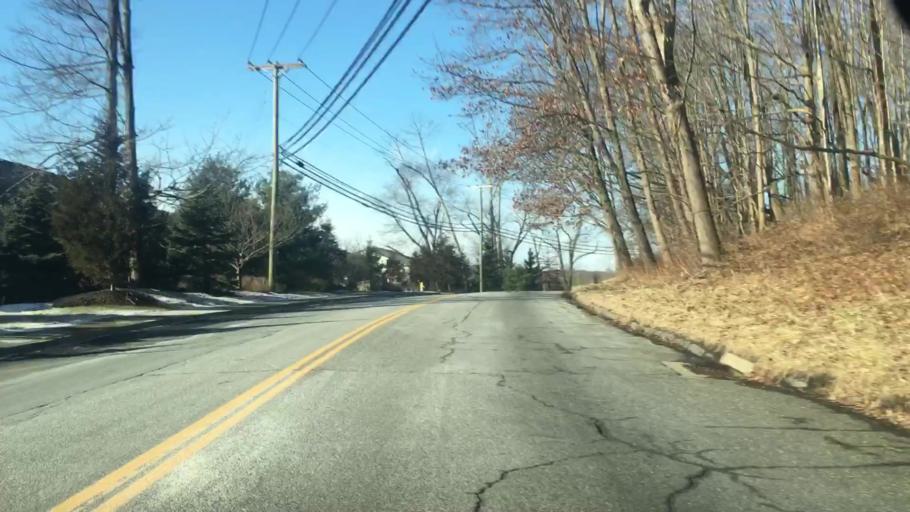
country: US
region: New York
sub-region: Putnam County
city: Peach Lake
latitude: 41.3792
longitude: -73.5343
